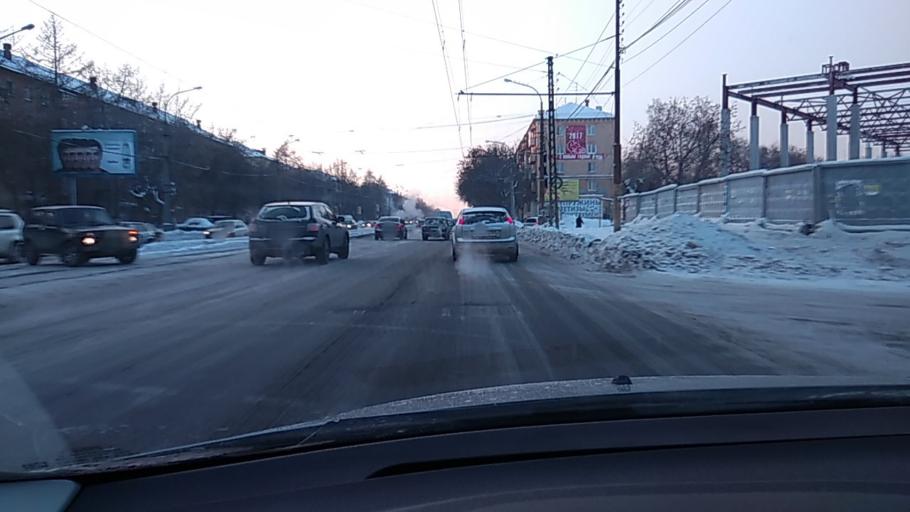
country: RU
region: Sverdlovsk
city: Yekaterinburg
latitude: 56.8854
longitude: 60.5844
